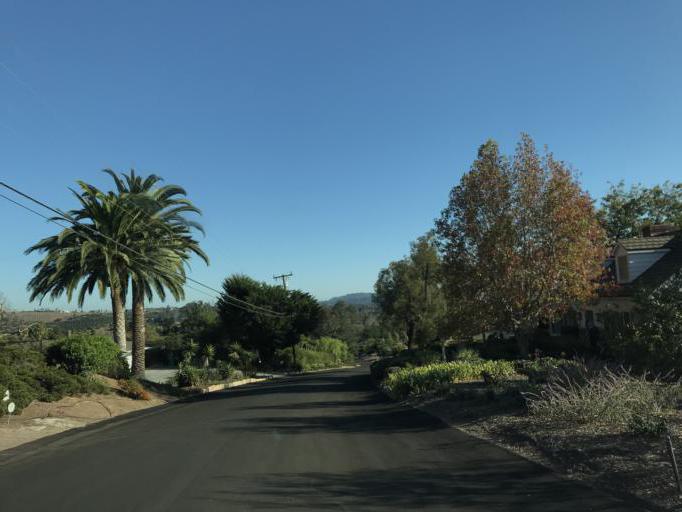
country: US
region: California
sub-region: Santa Barbara County
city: Goleta
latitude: 34.4617
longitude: -119.8196
